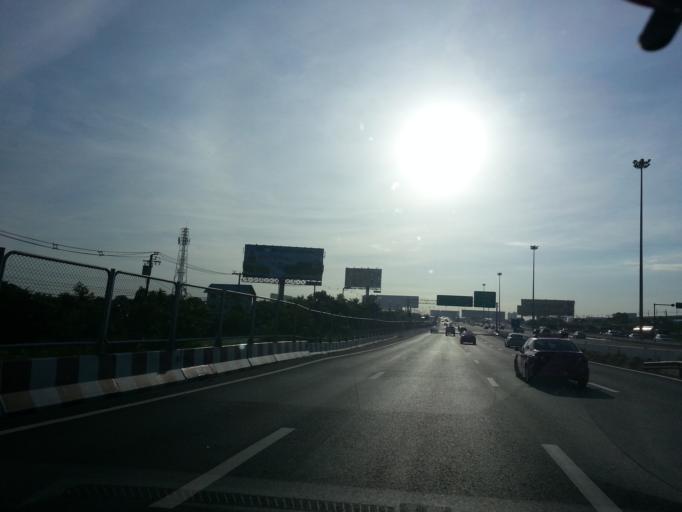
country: TH
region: Bangkok
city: Lat Krabang
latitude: 13.7299
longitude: 100.7488
